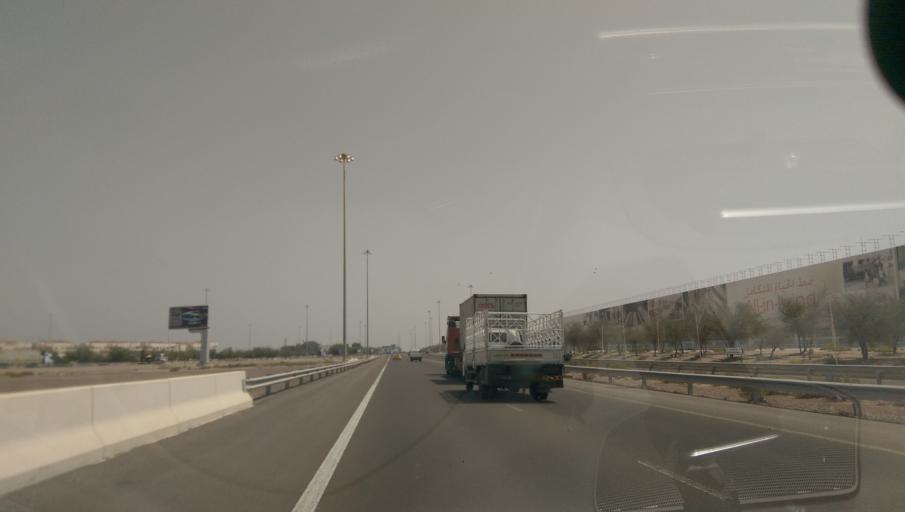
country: AE
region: Abu Dhabi
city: Abu Dhabi
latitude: 24.5451
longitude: 54.6940
